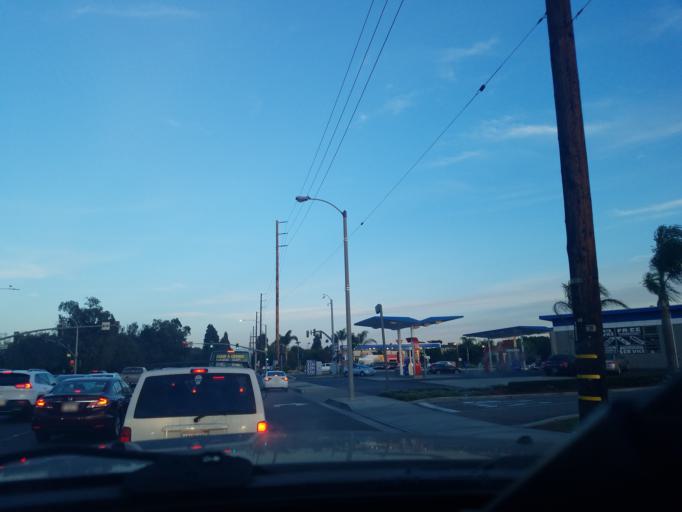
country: US
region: California
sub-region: Orange County
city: Fountain Valley
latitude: 33.7161
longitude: -117.9554
